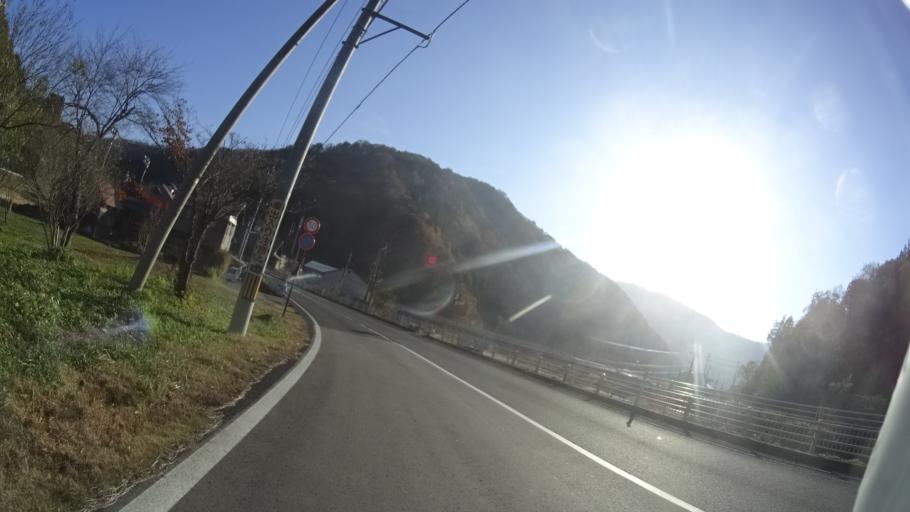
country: JP
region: Fukui
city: Ono
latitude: 35.9072
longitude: 136.6696
